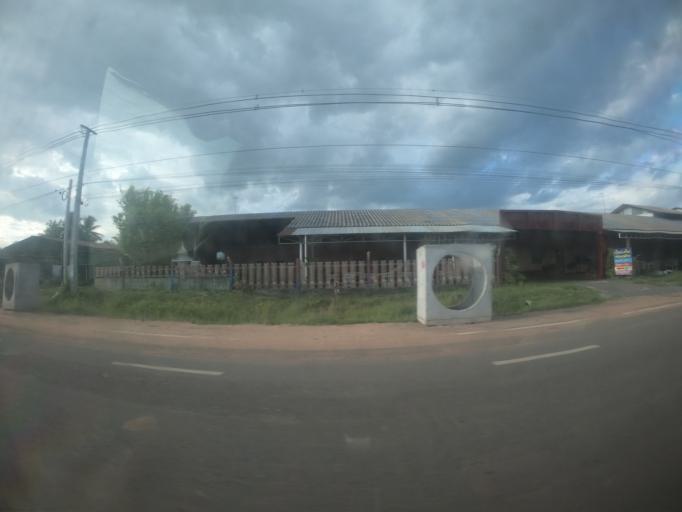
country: TH
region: Surin
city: Kap Choeng
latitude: 14.4555
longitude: 103.6811
